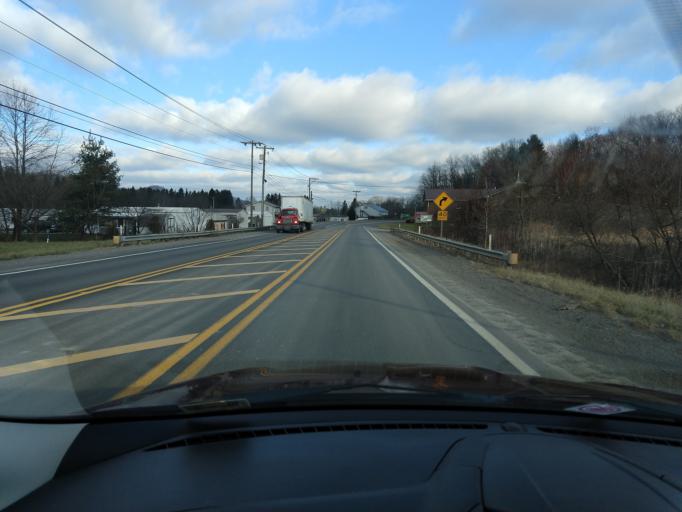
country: US
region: West Virginia
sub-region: Randolph County
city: Elkins
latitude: 38.8250
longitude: -79.8746
